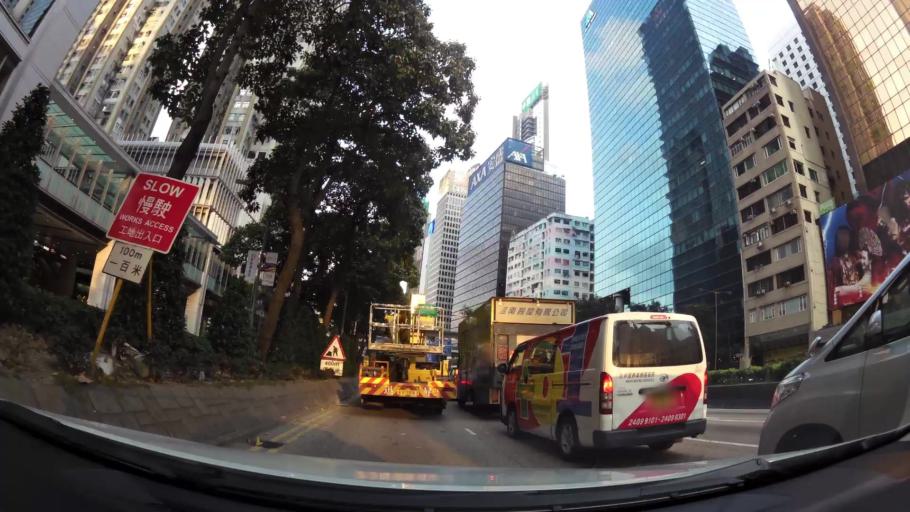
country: HK
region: Wanchai
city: Wan Chai
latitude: 22.2797
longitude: 114.1756
